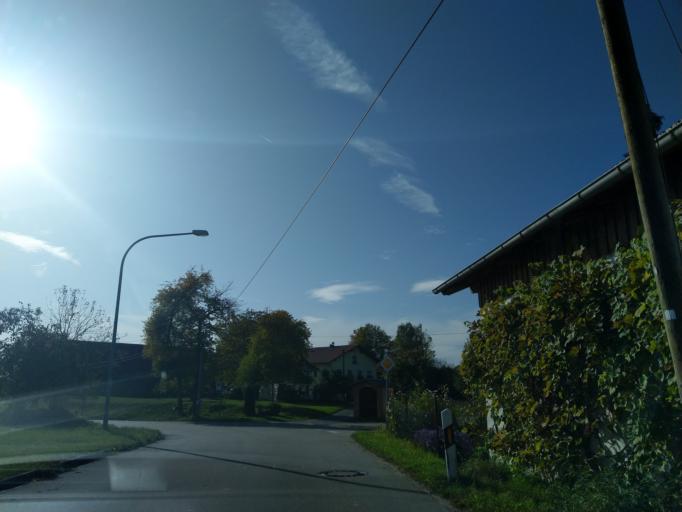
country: DE
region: Bavaria
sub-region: Lower Bavaria
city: Bernried
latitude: 48.9068
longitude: 12.8493
